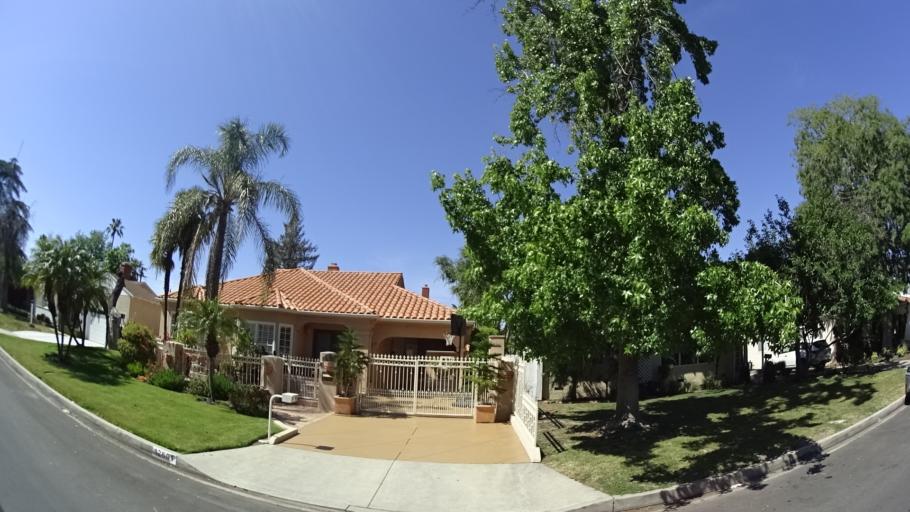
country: US
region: California
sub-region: Los Angeles County
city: North Hollywood
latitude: 34.1740
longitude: -118.4075
